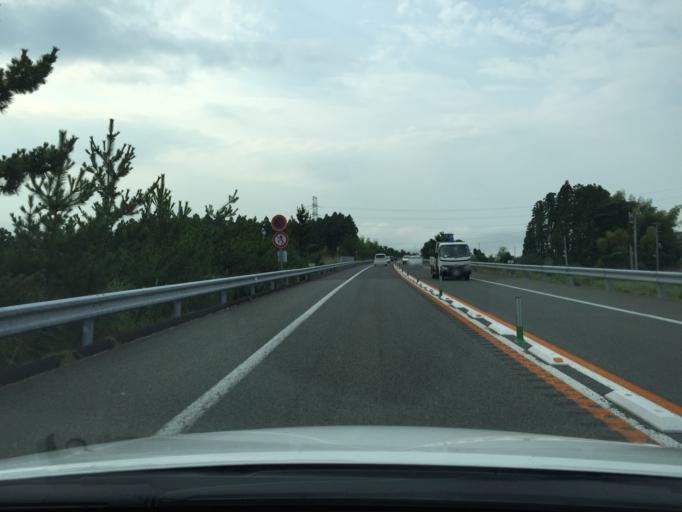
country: JP
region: Fukushima
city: Namie
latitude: 37.3583
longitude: 140.9727
